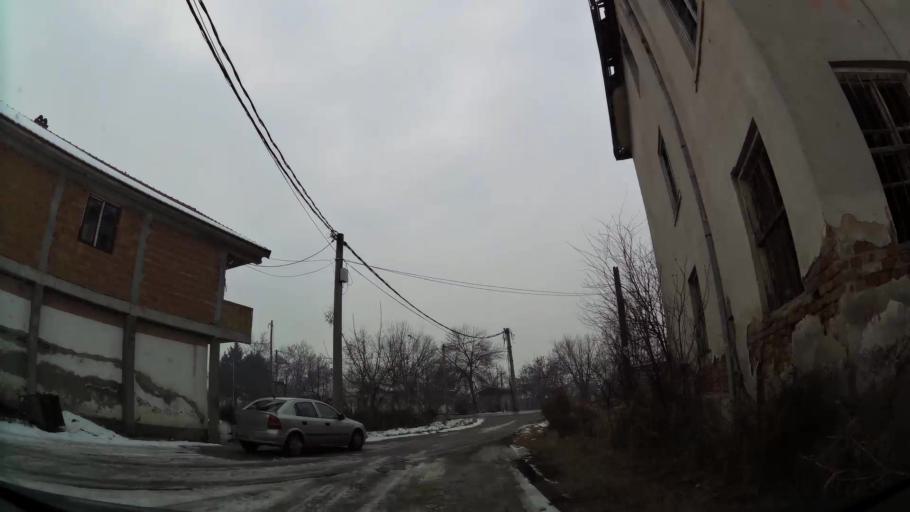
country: MK
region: Petrovec
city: Petrovec
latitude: 41.9388
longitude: 21.6169
